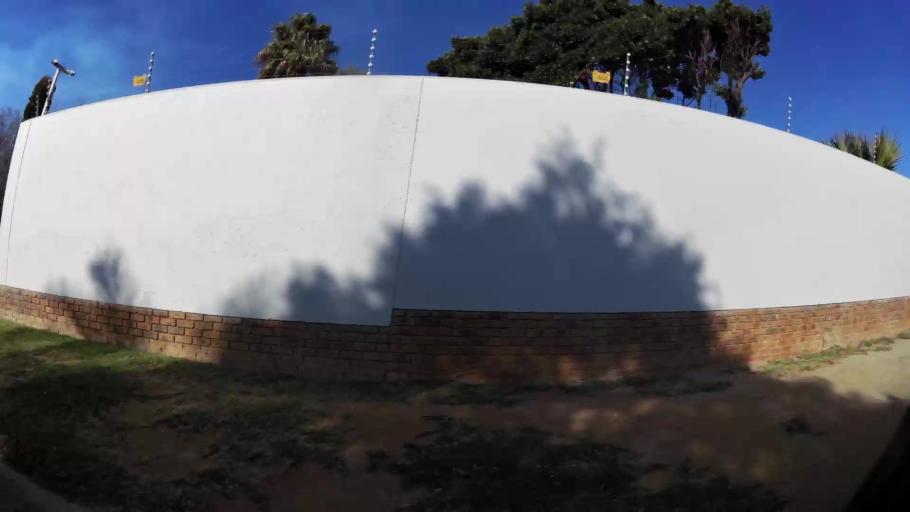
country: ZA
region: Gauteng
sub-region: City of Johannesburg Metropolitan Municipality
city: Roodepoort
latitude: -26.0992
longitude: 27.9731
